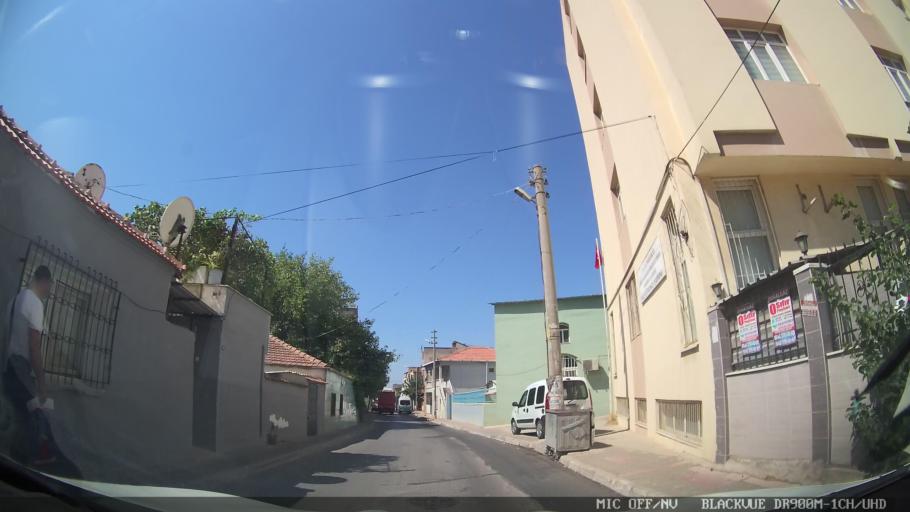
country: TR
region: Izmir
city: Karsiyaka
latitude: 38.4976
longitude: 27.0678
